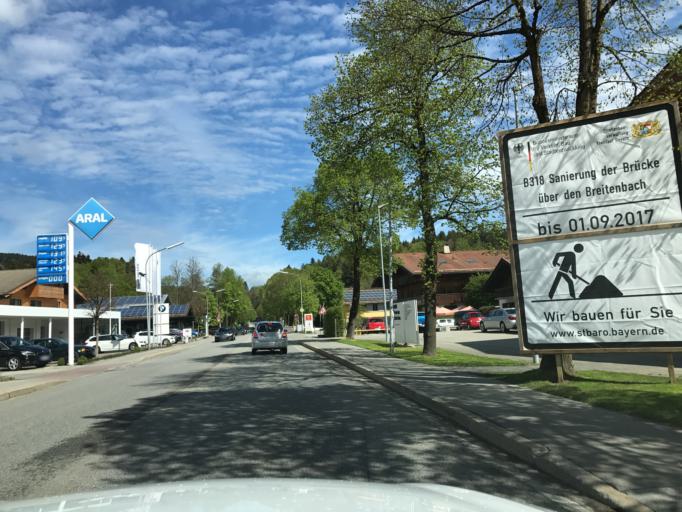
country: DE
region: Bavaria
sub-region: Upper Bavaria
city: Bad Wiessee
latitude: 47.7178
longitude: 11.7193
